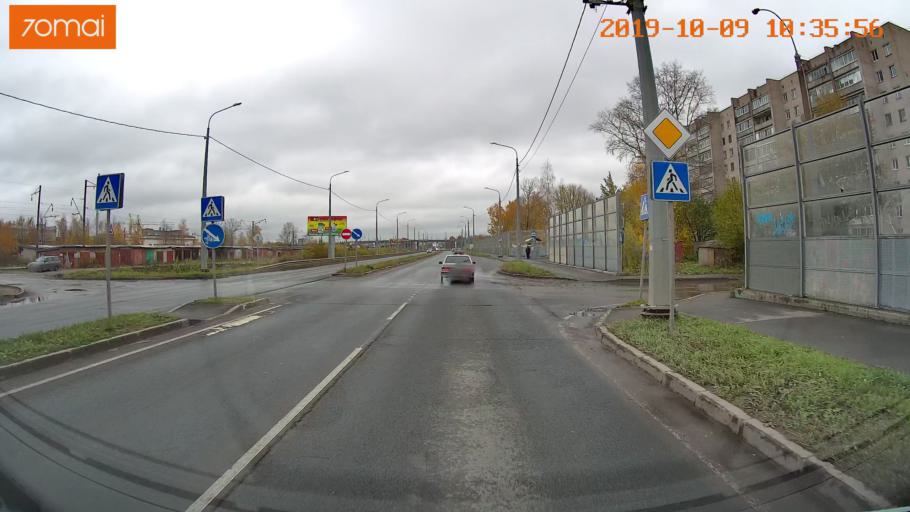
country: RU
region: Vologda
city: Vologda
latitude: 59.2292
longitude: 39.8624
